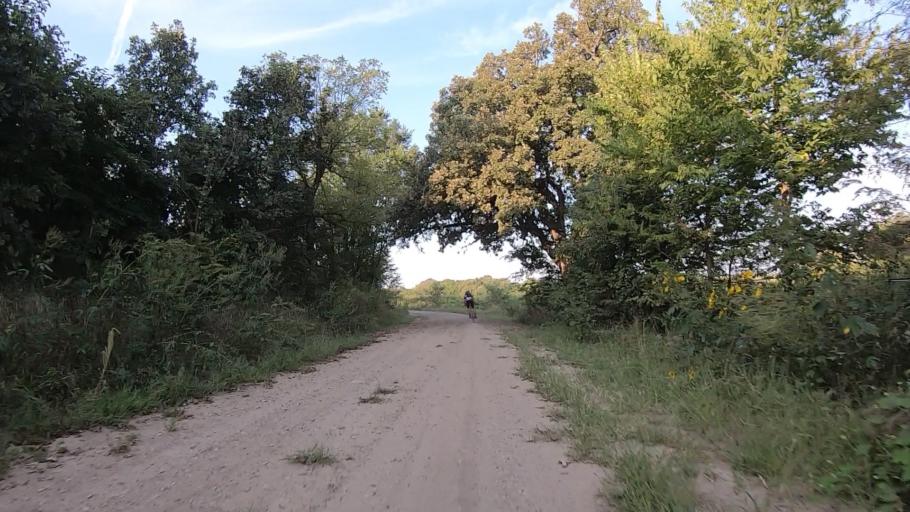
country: US
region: Kansas
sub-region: Marshall County
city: Blue Rapids
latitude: 39.7476
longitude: -96.7528
